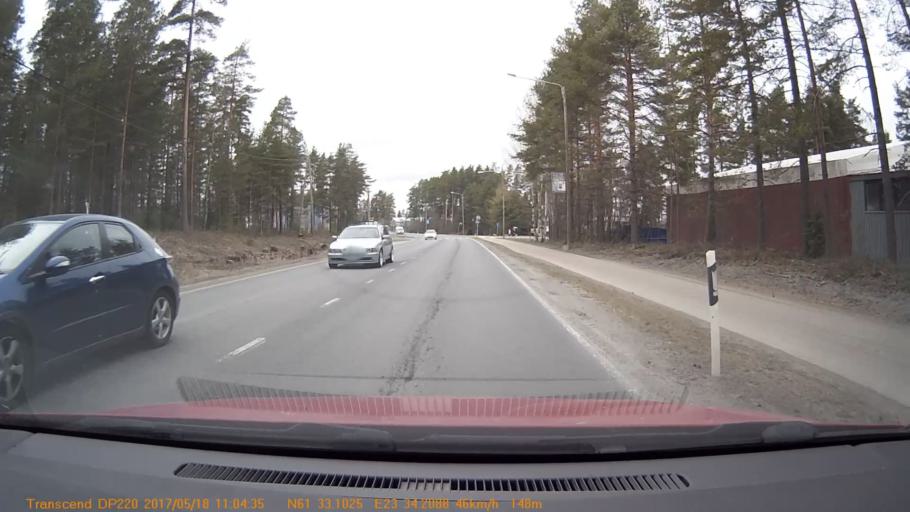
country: FI
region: Pirkanmaa
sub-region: Tampere
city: Yloejaervi
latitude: 61.5516
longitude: 23.5705
